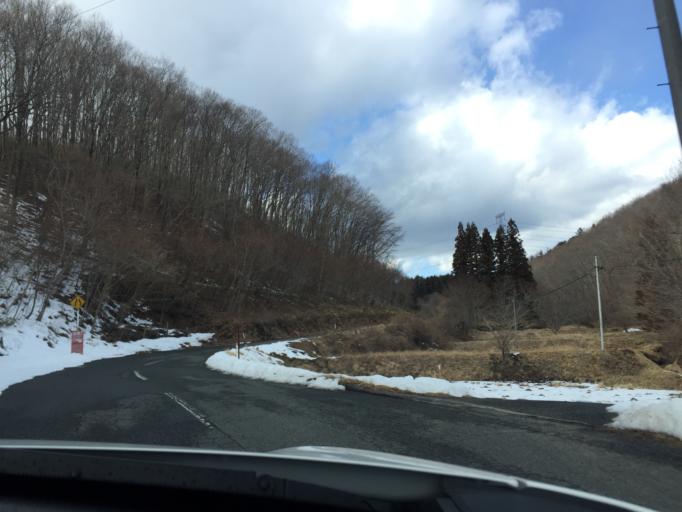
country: JP
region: Fukushima
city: Funehikimachi-funehiki
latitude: 37.2736
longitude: 140.7259
